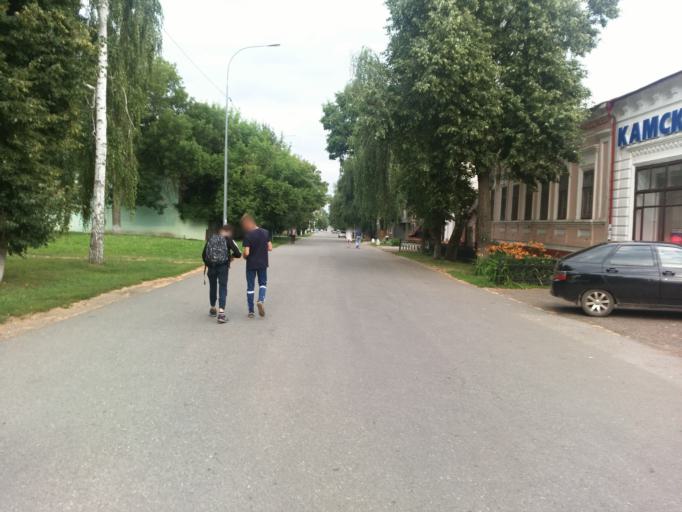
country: RU
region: Tatarstan
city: Yelabuga
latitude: 55.7552
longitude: 52.0655
